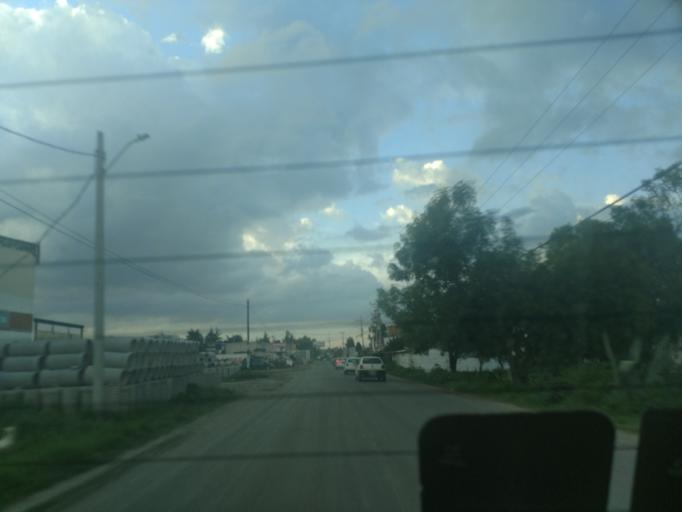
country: MX
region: Mexico
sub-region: Cuautitlan
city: Barrio Tlatenco
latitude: 19.7520
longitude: -99.2007
